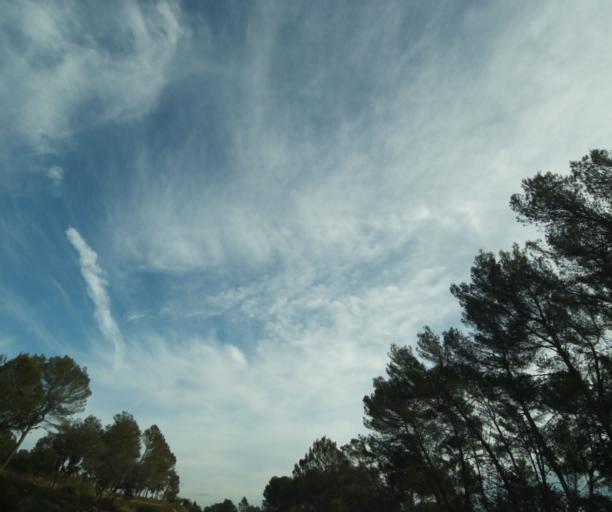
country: FR
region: Provence-Alpes-Cote d'Azur
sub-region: Departement du Var
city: La Celle
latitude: 43.4187
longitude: 6.0204
